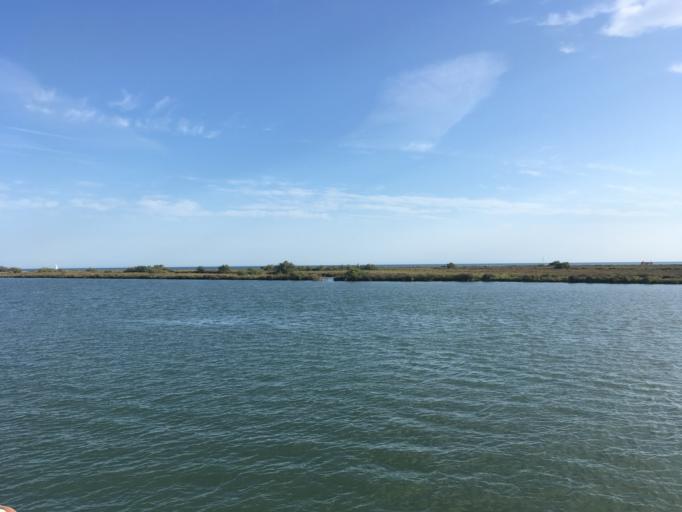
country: FR
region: Provence-Alpes-Cote d'Azur
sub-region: Departement des Bouches-du-Rhone
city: Saintes-Maries-de-la-Mer
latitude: 43.4566
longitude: 4.3910
